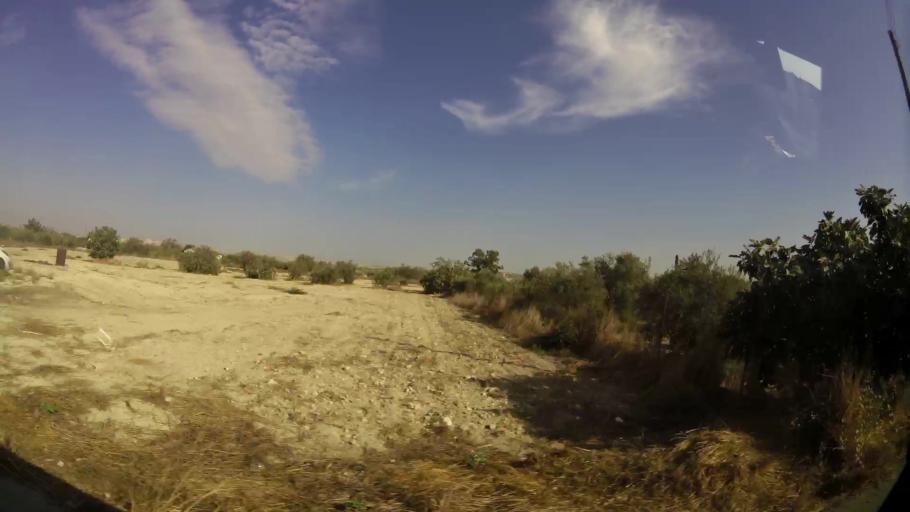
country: CY
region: Larnaka
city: Aradippou
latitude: 34.9527
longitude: 33.6061
